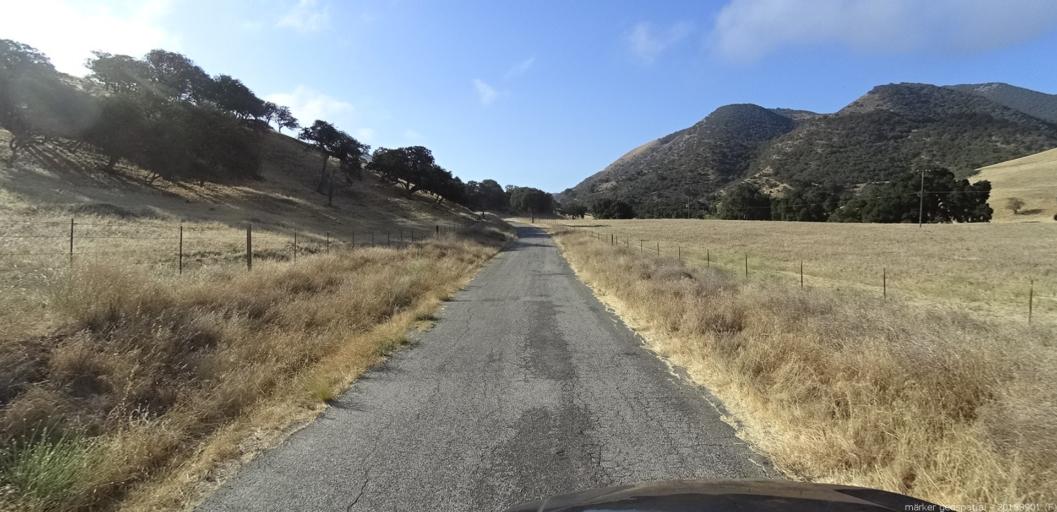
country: US
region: California
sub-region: Monterey County
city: Greenfield
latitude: 36.2451
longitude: -121.2872
